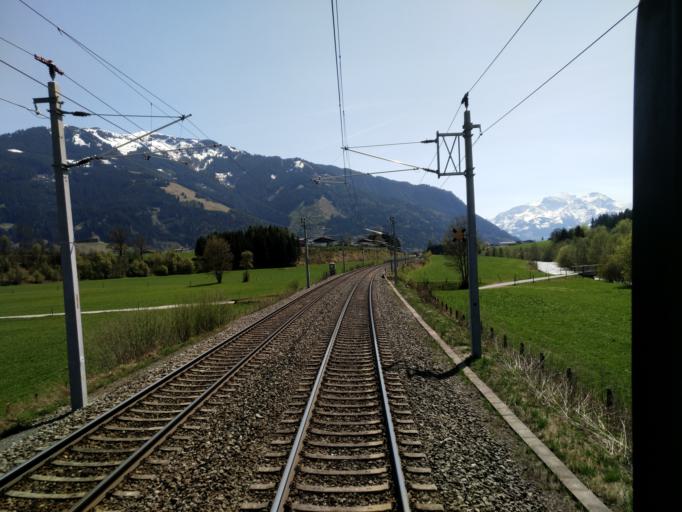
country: AT
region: Salzburg
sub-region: Politischer Bezirk Zell am See
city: Saalfelden am Steinernen Meer
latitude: 47.4043
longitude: 12.8292
